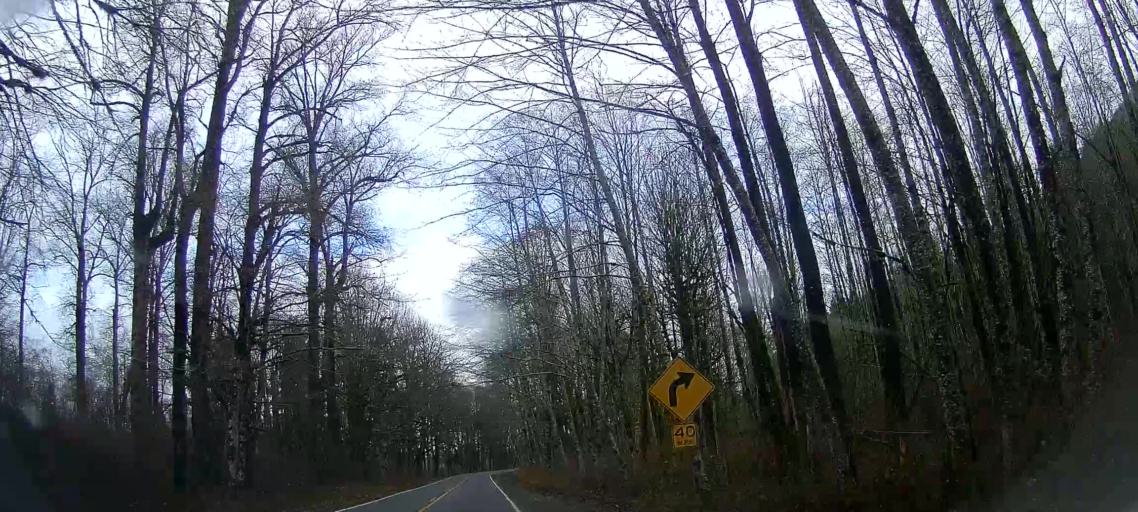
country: US
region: Washington
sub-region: Skagit County
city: Sedro-Woolley
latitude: 48.5163
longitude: -121.9674
